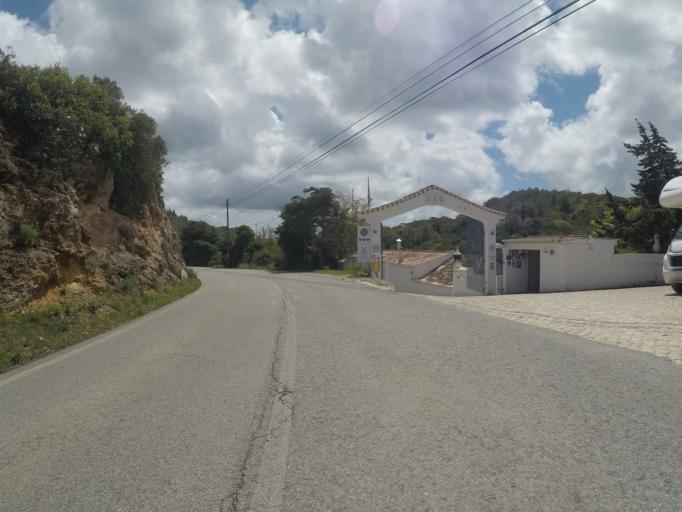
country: PT
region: Faro
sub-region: Vila do Bispo
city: Vila do Bispo
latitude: 37.0754
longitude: -8.8314
